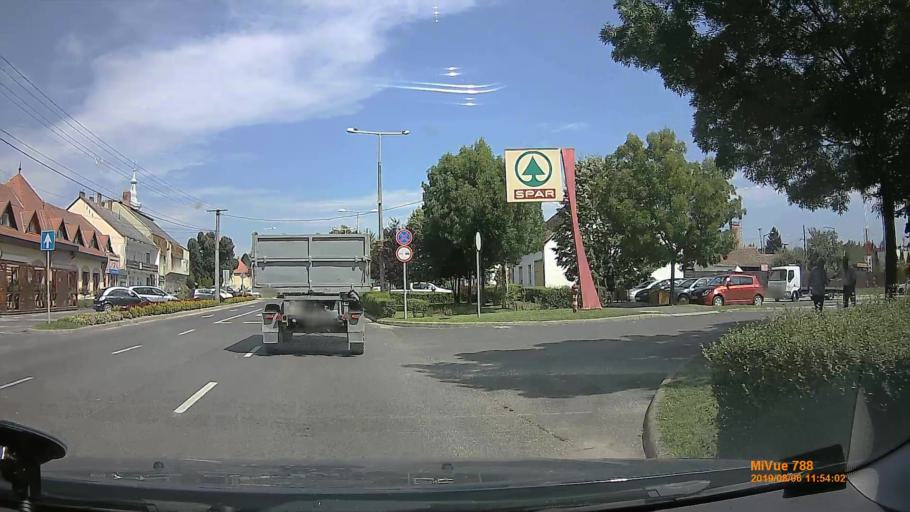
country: HU
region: Zala
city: Letenye
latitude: 46.4322
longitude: 16.7223
